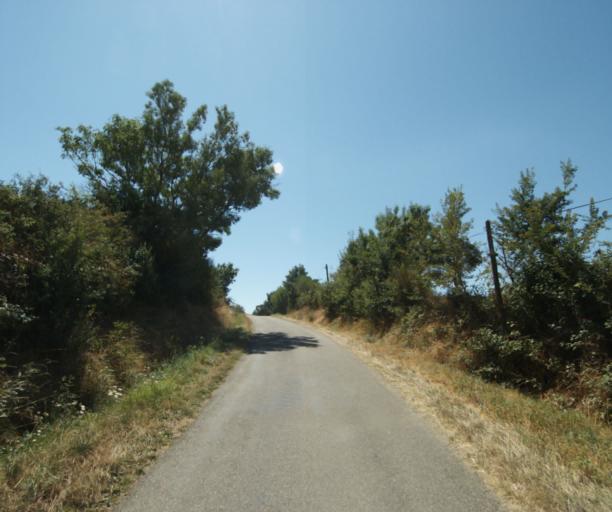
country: FR
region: Midi-Pyrenees
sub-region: Departement de la Haute-Garonne
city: Saint-Felix-Lauragais
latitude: 43.4566
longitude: 1.8990
